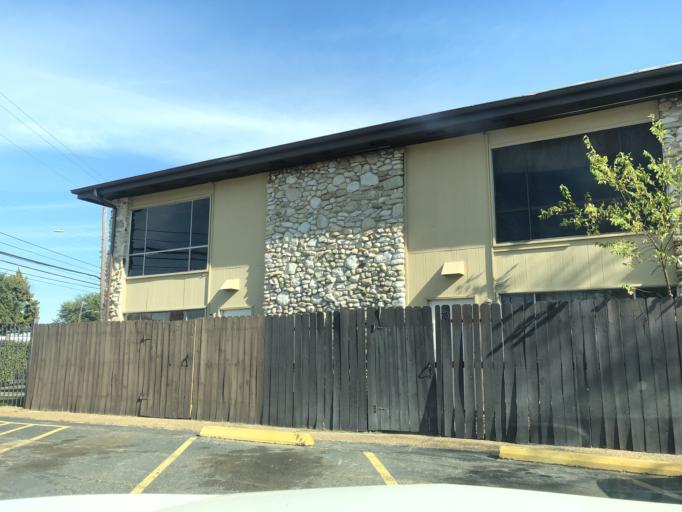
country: US
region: Texas
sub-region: Harris County
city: Bellaire
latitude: 29.6872
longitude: -95.5074
